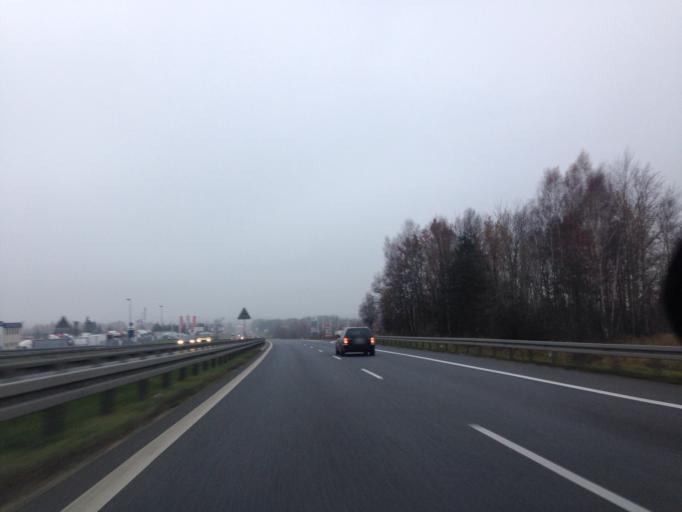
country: PL
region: Lodz Voivodeship
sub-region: Powiat lodzki wschodni
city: Rzgow
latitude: 51.6737
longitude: 19.4757
